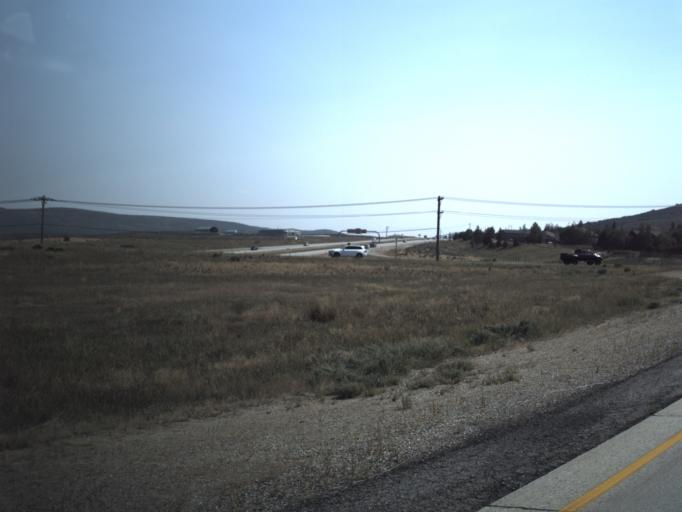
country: US
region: Utah
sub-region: Summit County
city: Snyderville
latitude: 40.7180
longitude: -111.4886
